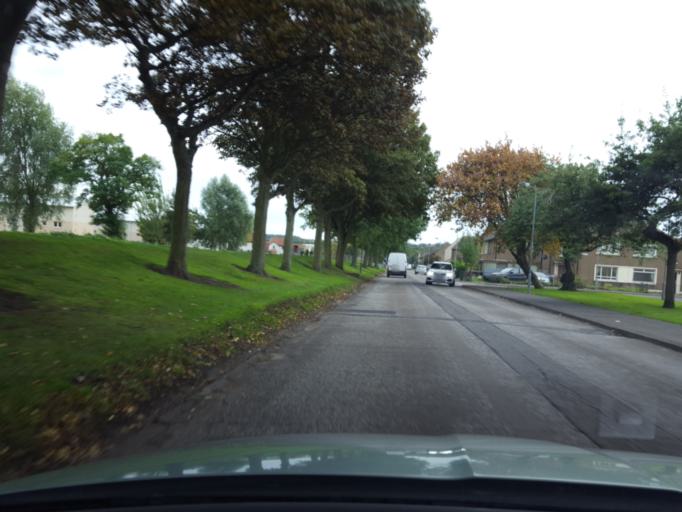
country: GB
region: Scotland
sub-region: Falkirk
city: Grangemouth
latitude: 56.0085
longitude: -3.7240
